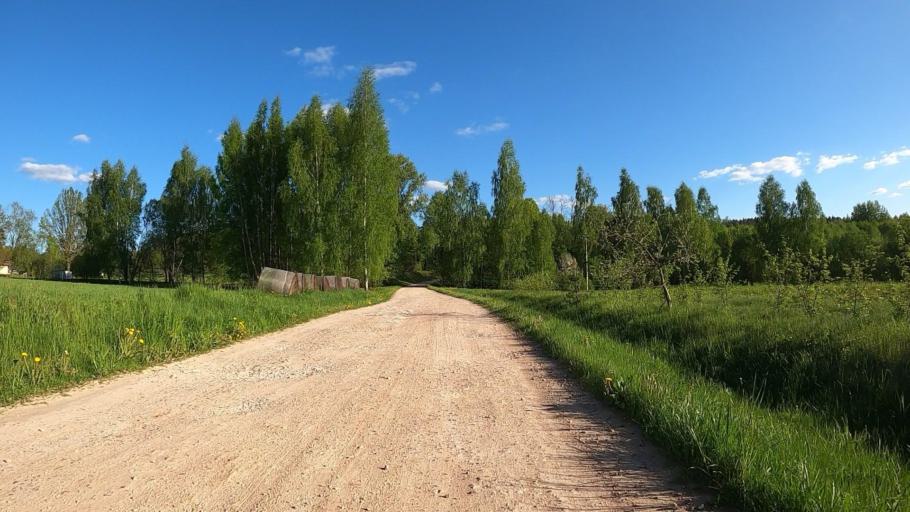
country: LV
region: Baldone
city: Baldone
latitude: 56.7700
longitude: 24.3354
